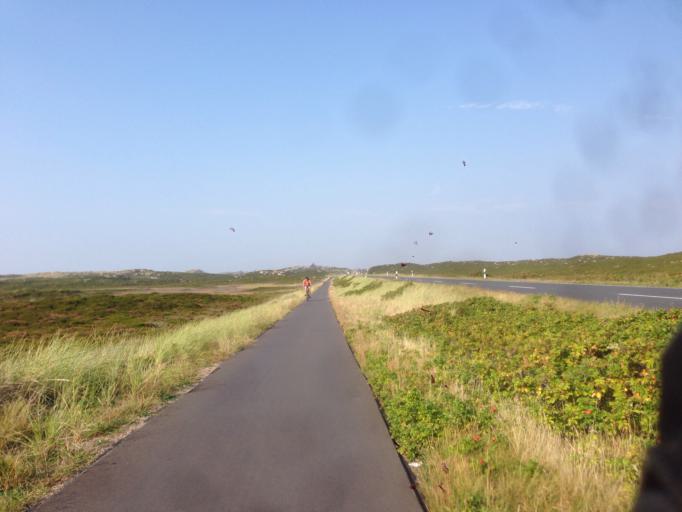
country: DE
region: Schleswig-Holstein
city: Westerland
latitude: 54.8321
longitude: 8.2914
